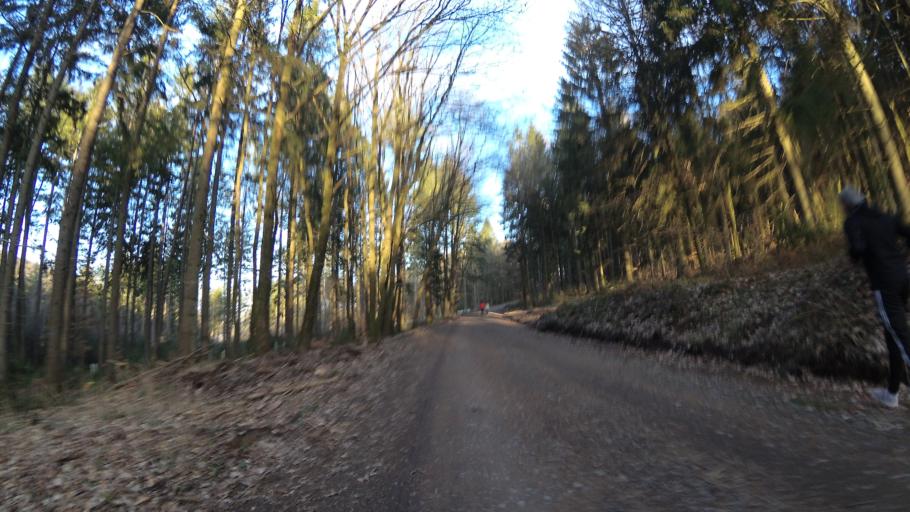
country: DE
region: Saarland
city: Eppelborn
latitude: 49.4111
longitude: 6.9849
